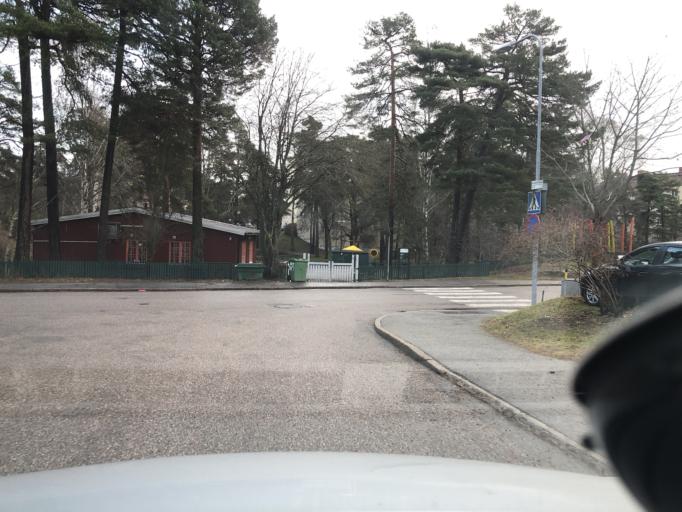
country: SE
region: Stockholm
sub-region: Stockholms Kommun
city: Arsta
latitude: 59.2973
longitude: 18.0592
